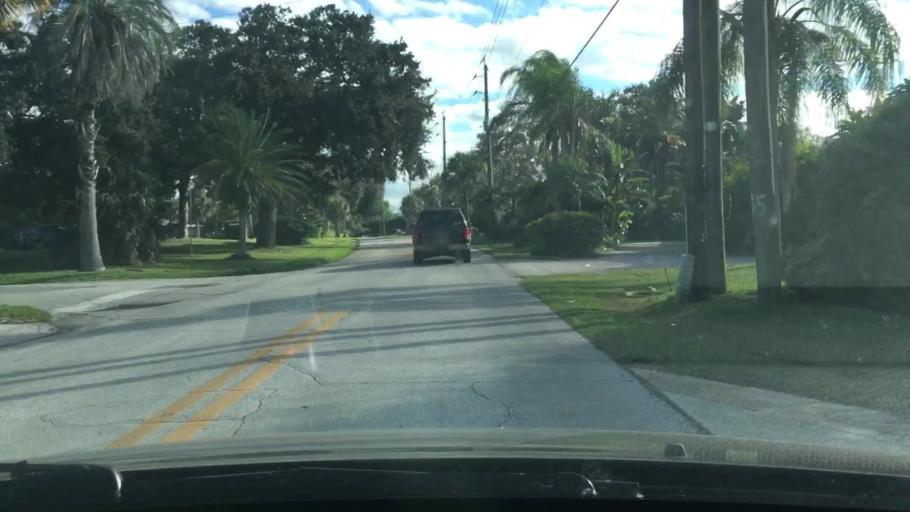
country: US
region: Florida
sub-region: Volusia County
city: Ormond-by-the-Sea
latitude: 29.3224
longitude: -81.0630
